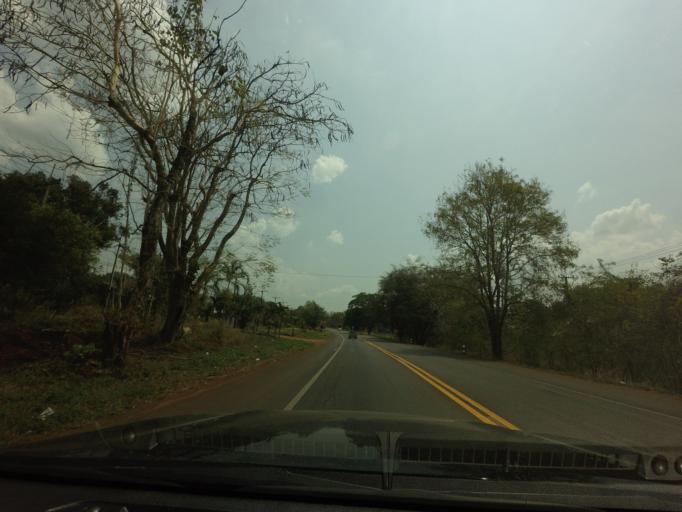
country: TH
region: Kanchanaburi
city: Sai Yok
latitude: 14.1378
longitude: 99.1501
